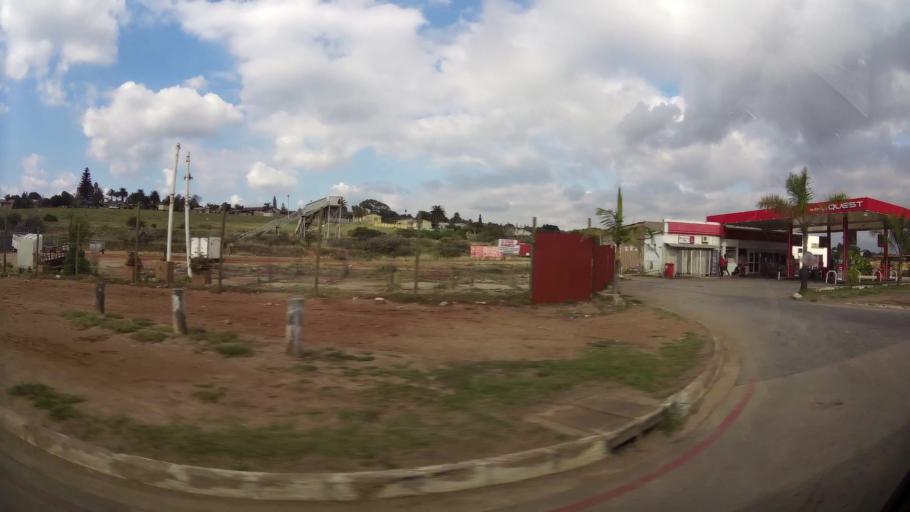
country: ZA
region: Eastern Cape
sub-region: Nelson Mandela Bay Metropolitan Municipality
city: Uitenhage
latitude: -33.7512
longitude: 25.4137
